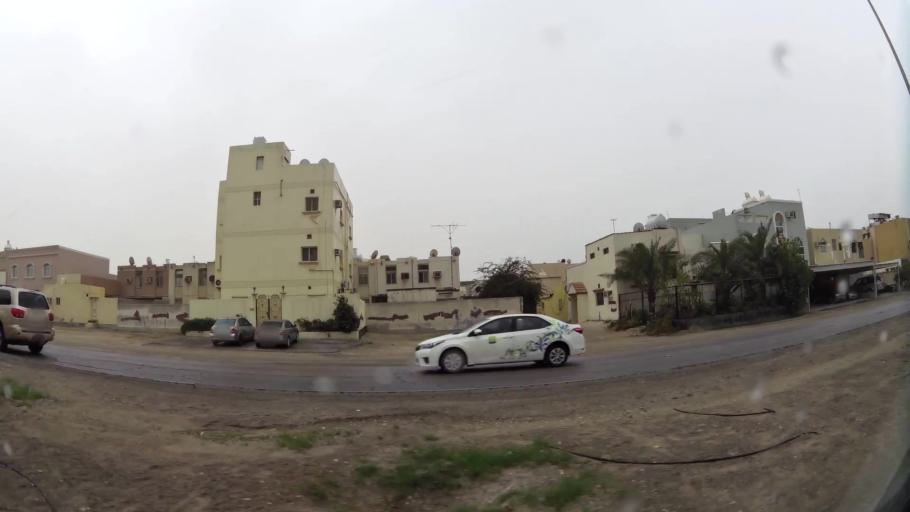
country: BH
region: Northern
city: Madinat `Isa
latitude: 26.1586
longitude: 50.5718
